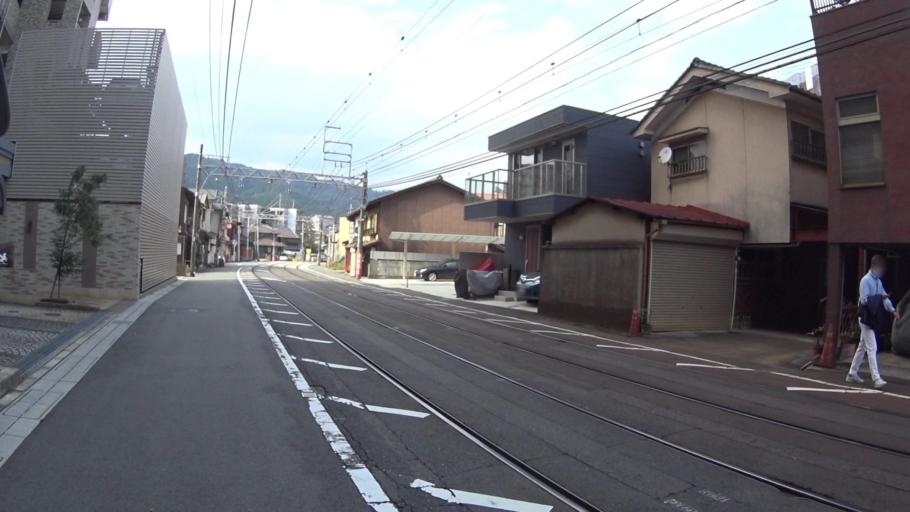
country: JP
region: Osaka
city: Izumiotsu
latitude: 34.5236
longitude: 135.3562
